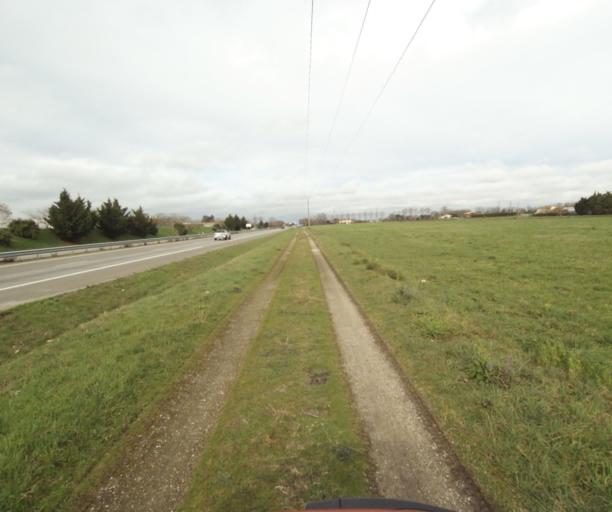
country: FR
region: Midi-Pyrenees
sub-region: Departement de l'Ariege
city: La Tour-du-Crieu
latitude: 43.1110
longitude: 1.6317
